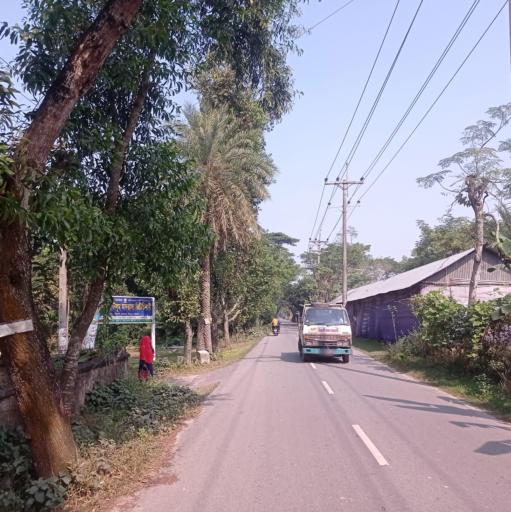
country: BD
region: Dhaka
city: Narsingdi
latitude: 24.0592
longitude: 90.6870
